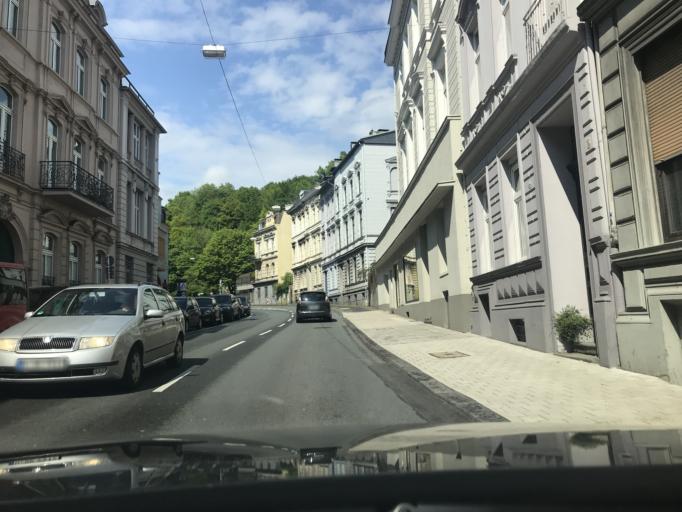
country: DE
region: North Rhine-Westphalia
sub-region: Regierungsbezirk Dusseldorf
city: Wuppertal
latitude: 51.2561
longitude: 7.1315
